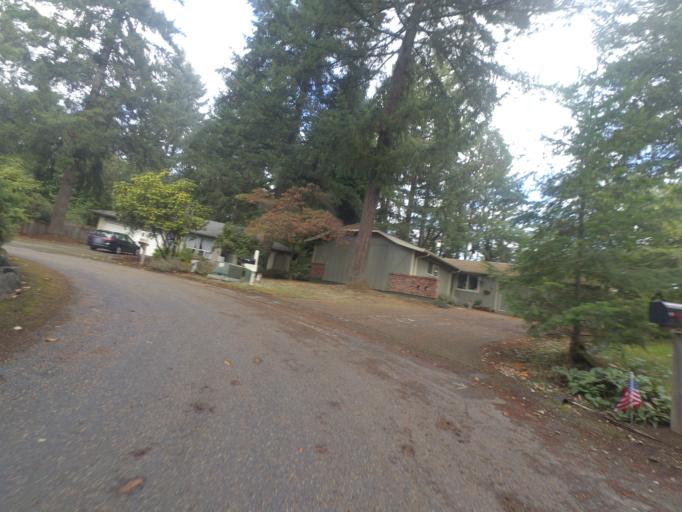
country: US
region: Washington
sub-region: Pierce County
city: University Place
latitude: 47.2140
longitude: -122.5522
